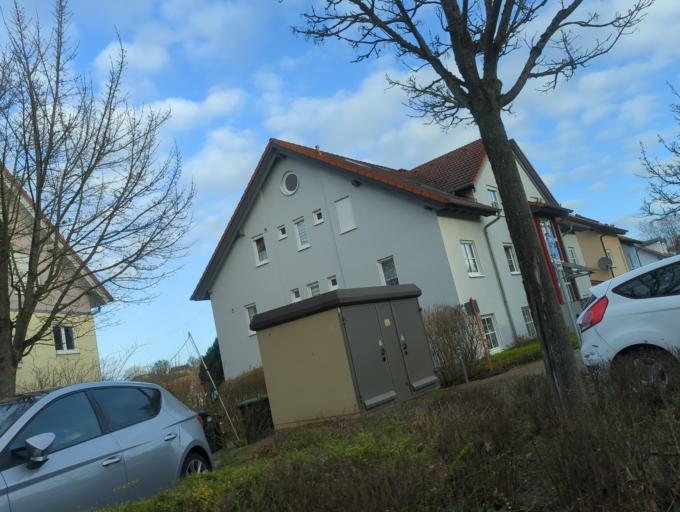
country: DE
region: Baden-Wuerttemberg
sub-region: Karlsruhe Region
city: Joehlingen
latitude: 49.0284
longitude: 8.5850
